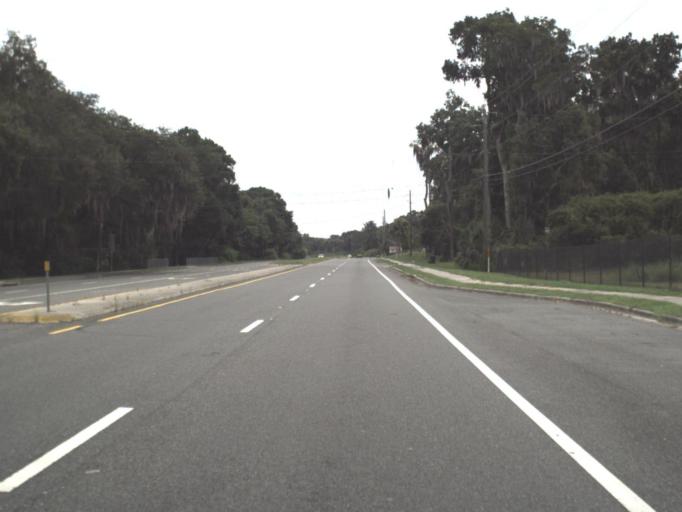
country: US
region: Florida
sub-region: Citrus County
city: Inverness
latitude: 28.8400
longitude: -82.3063
